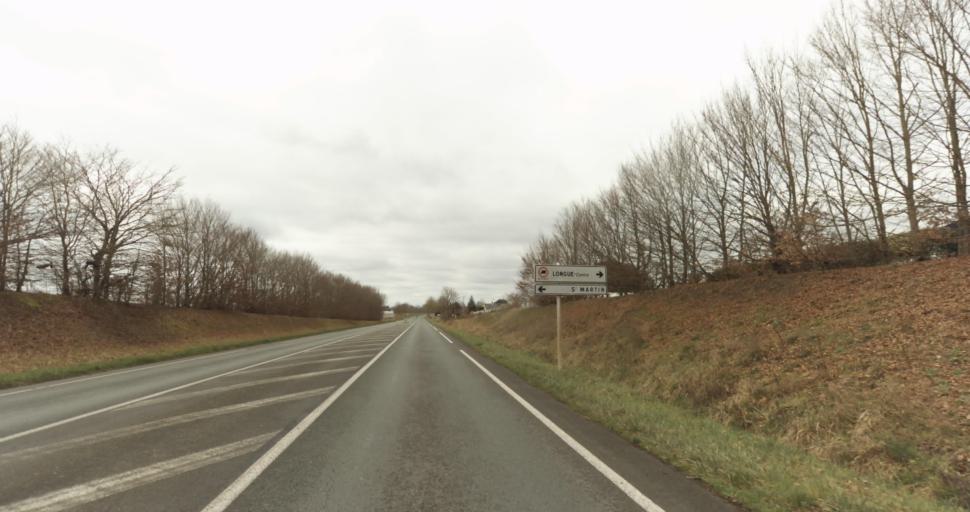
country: FR
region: Pays de la Loire
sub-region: Departement de Maine-et-Loire
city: Saint-Martin-de-la-Place
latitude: 47.3712
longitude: -0.1177
